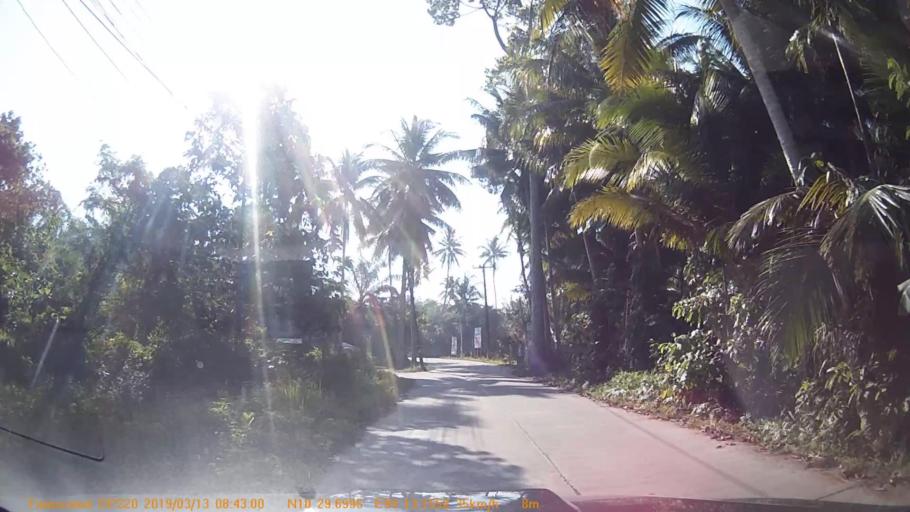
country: TH
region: Chumphon
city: Chumphon
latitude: 10.4950
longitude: 99.2193
